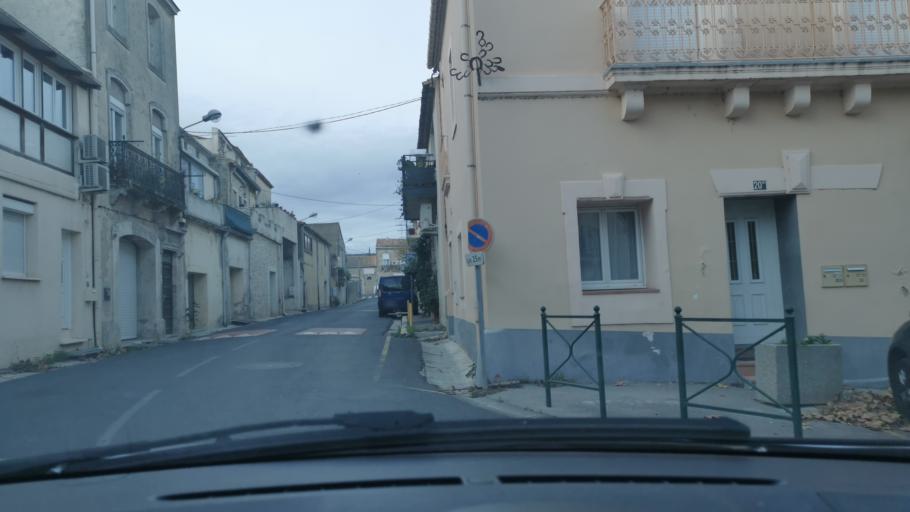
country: FR
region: Languedoc-Roussillon
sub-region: Departement de l'Herault
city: Mireval
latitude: 43.5085
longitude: 3.8030
